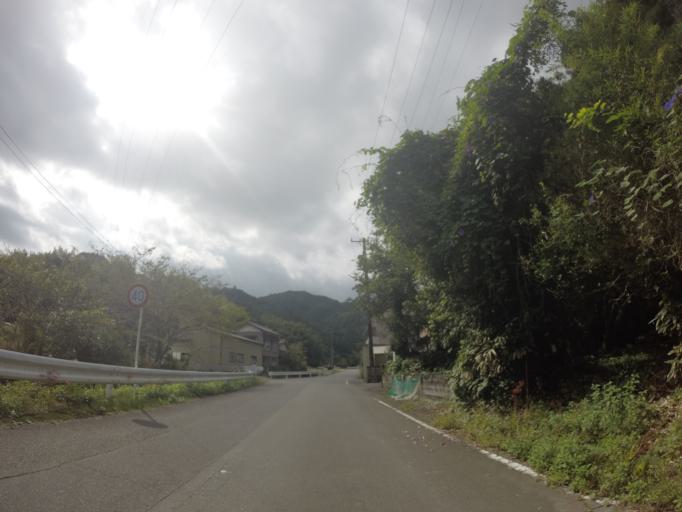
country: JP
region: Shizuoka
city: Fujieda
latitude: 34.9197
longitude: 138.2322
